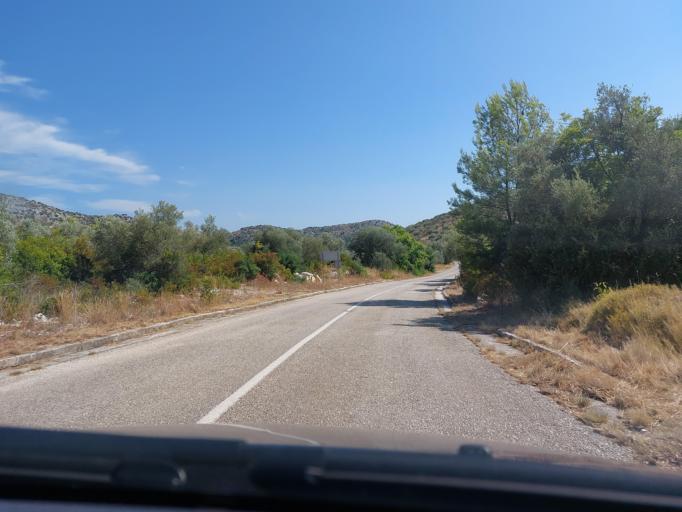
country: HR
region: Dubrovacko-Neretvanska
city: Smokvica
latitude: 42.7427
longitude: 16.8838
